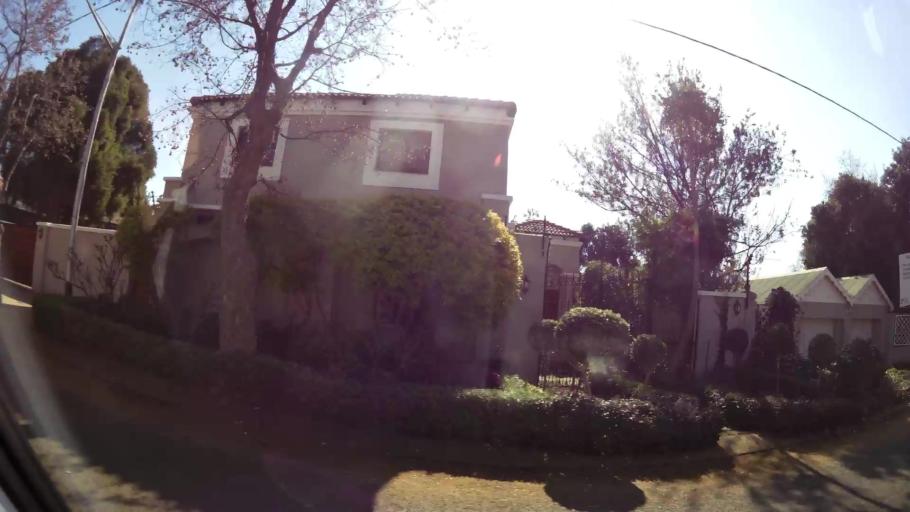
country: ZA
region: Gauteng
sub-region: City of Tshwane Metropolitan Municipality
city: Pretoria
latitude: -25.7653
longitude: 28.2557
